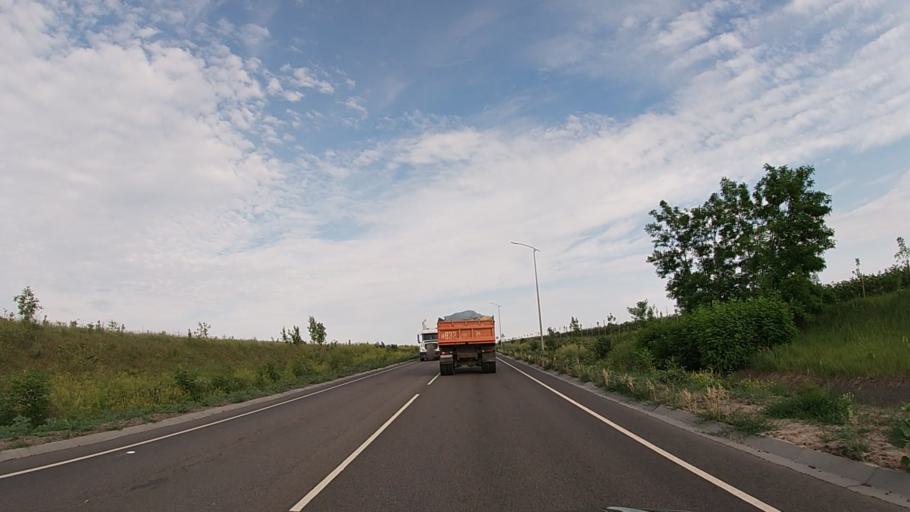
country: RU
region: Belgorod
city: Severnyy
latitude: 50.6706
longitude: 36.4843
